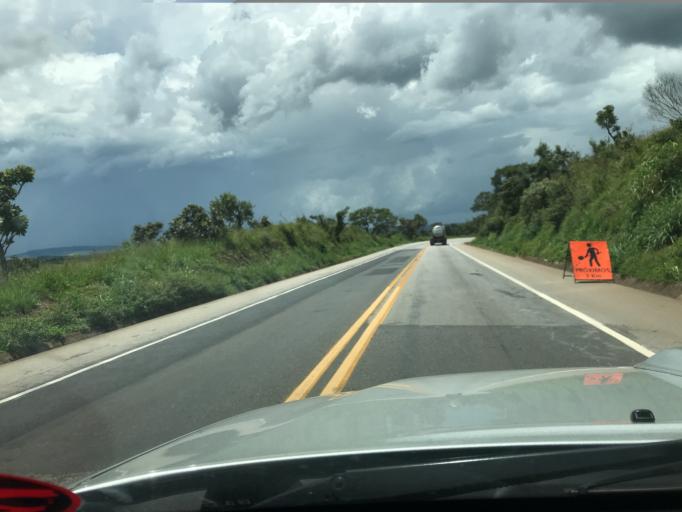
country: BR
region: Minas Gerais
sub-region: Ibia
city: Ibia
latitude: -19.5901
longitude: -46.4791
